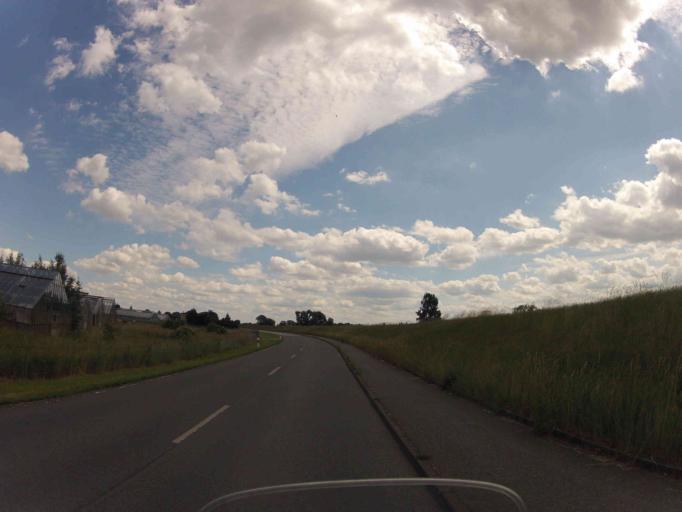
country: DE
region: Lower Saxony
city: Stelle
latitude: 53.4279
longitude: 10.1158
